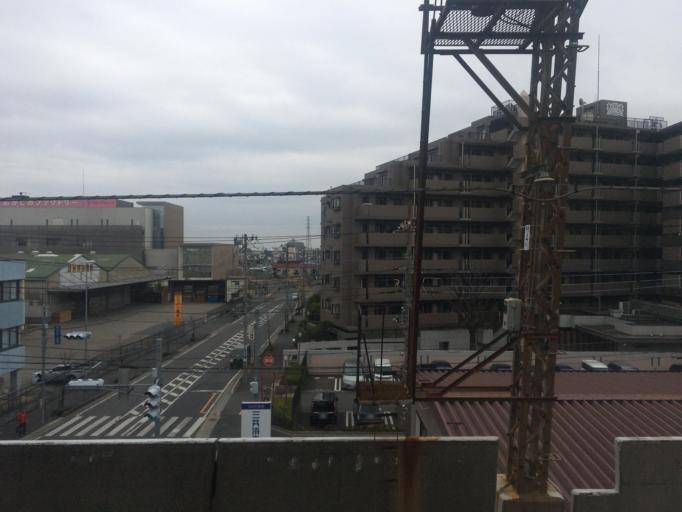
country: JP
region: Saitama
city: Shiki
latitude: 35.8409
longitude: 139.6228
